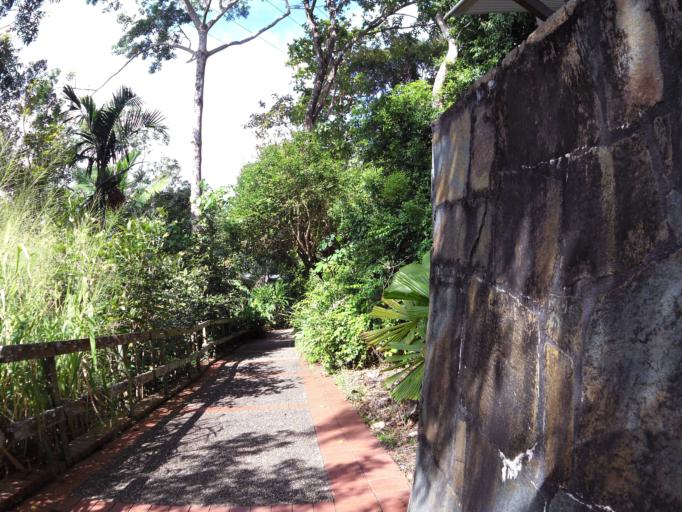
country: AU
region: Queensland
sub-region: Tablelands
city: Kuranda
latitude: -16.8181
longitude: 145.6378
